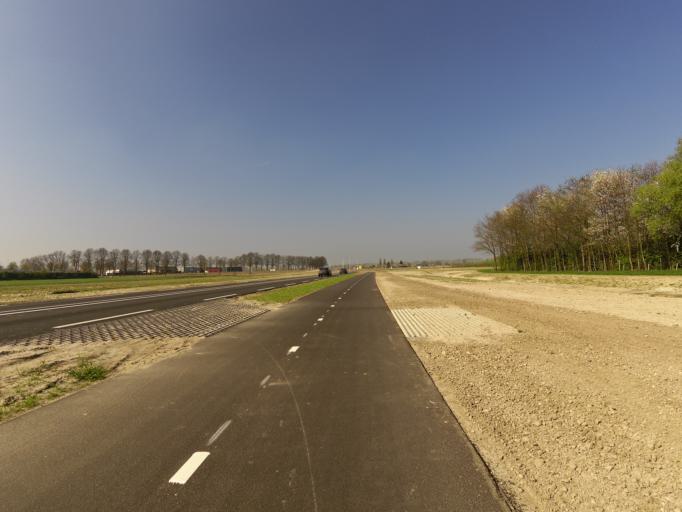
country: NL
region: Gelderland
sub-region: Gemeente Bronckhorst
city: Baak
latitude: 52.0678
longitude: 6.1956
